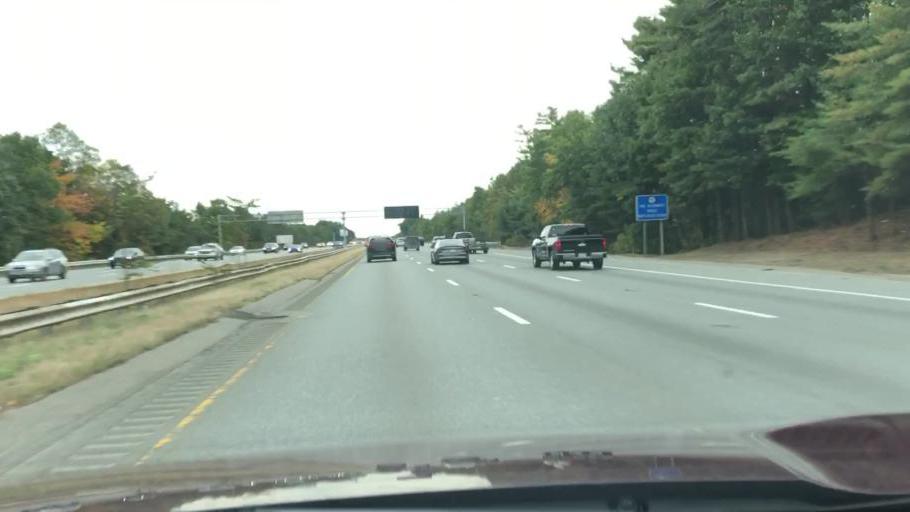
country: US
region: Massachusetts
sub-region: Essex County
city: Andover
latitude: 42.6132
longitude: -71.1745
